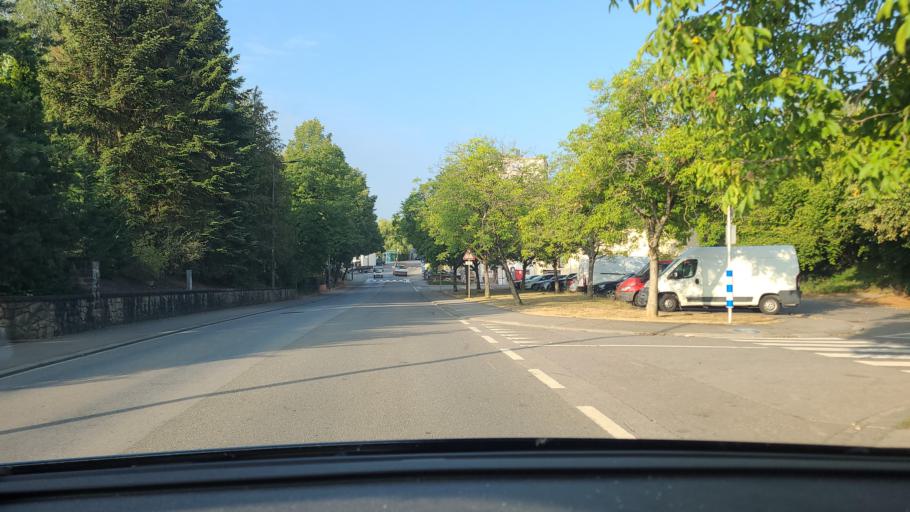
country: LU
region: Luxembourg
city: Hautcharage
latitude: 49.5781
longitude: 5.9112
